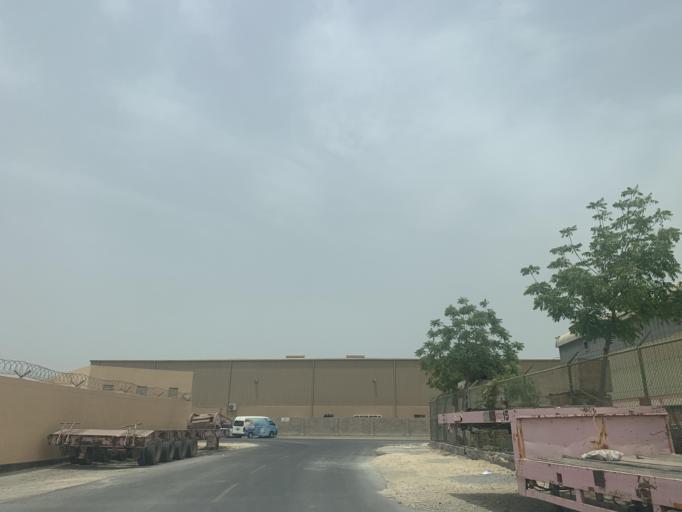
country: BH
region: Northern
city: Sitrah
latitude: 26.1770
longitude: 50.6218
